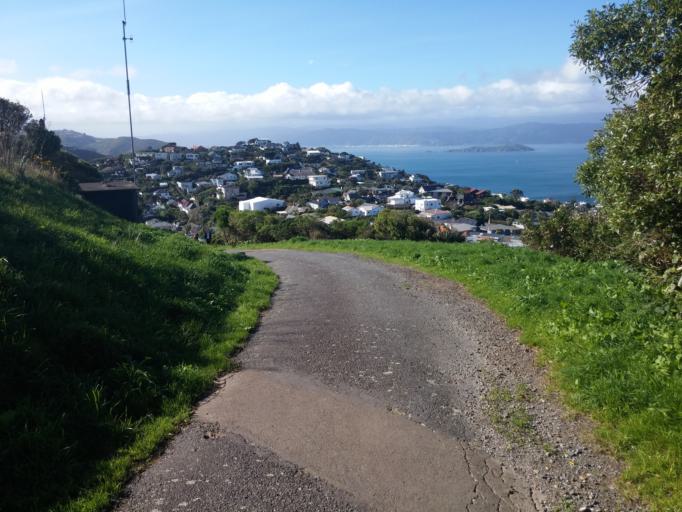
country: NZ
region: Wellington
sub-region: Wellington City
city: Wellington
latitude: -41.2533
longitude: 174.7839
